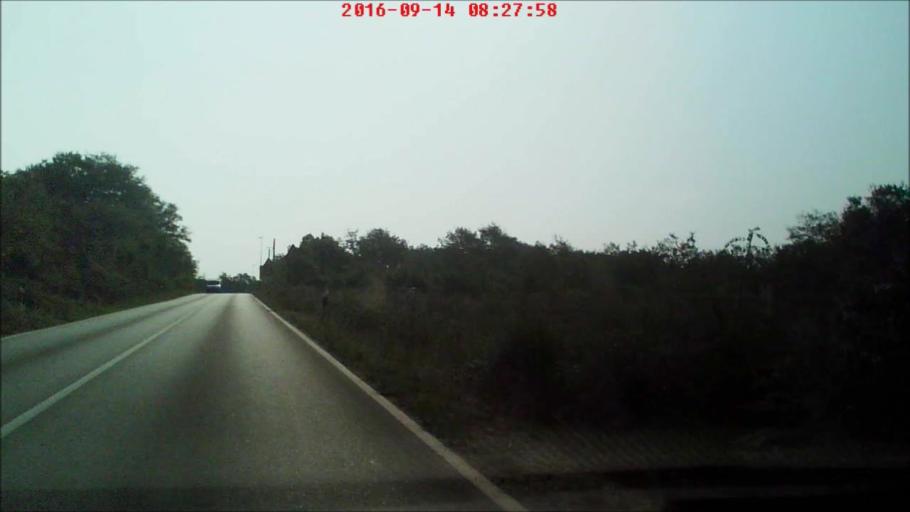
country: HR
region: Zadarska
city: Zadar
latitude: 44.1862
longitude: 15.2720
